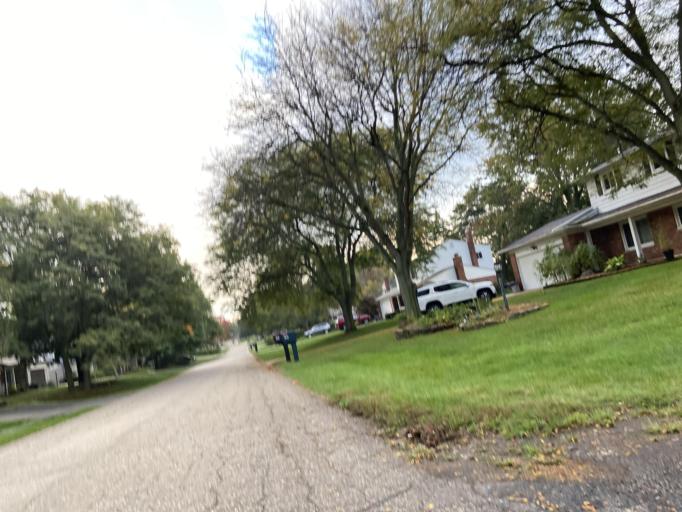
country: US
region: Michigan
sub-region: Oakland County
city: West Bloomfield Township
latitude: 42.5380
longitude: -83.3575
